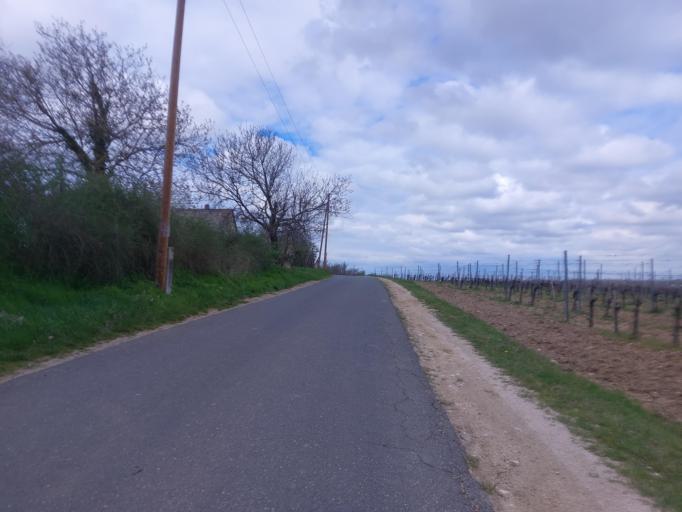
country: HU
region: Veszprem
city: Devecser
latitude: 47.1457
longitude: 17.3876
